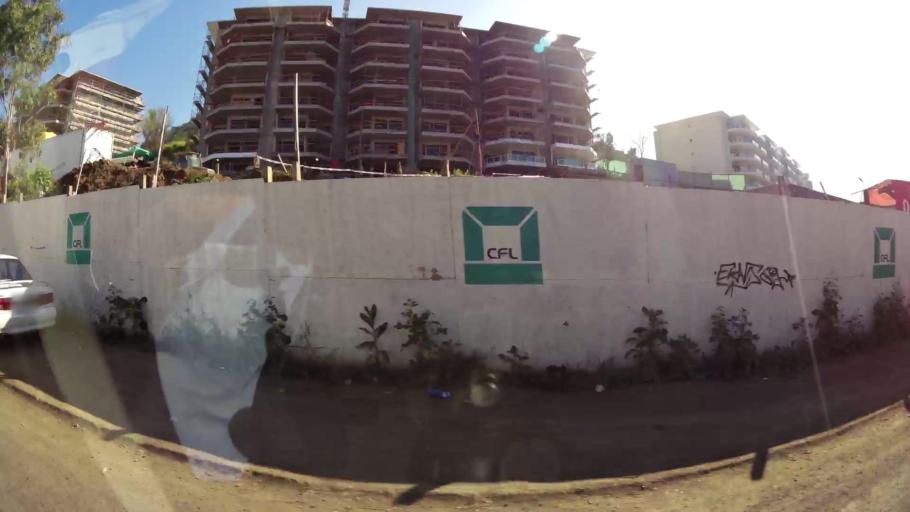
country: CL
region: Santiago Metropolitan
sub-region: Provincia de Chacabuco
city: Chicureo Abajo
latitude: -33.3396
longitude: -70.6708
